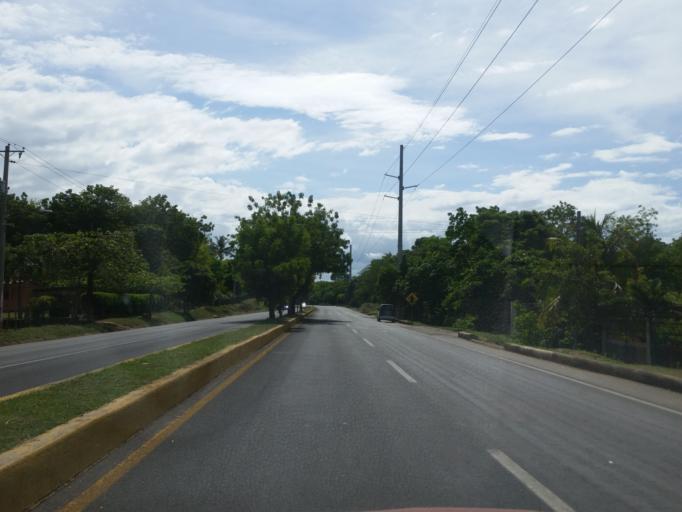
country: NI
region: Masaya
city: Masaya
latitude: 11.9752
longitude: -86.0324
